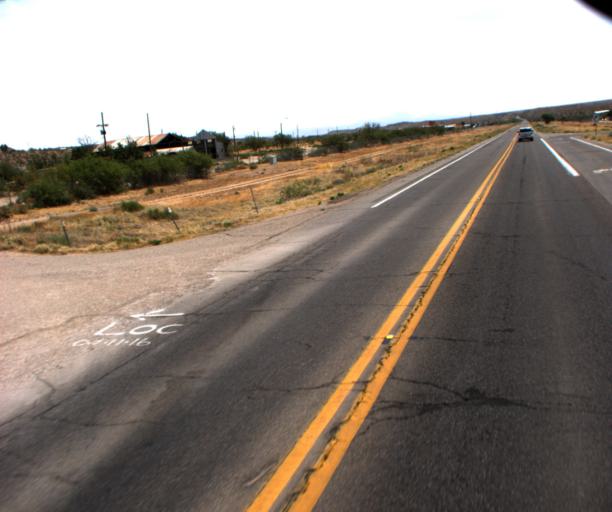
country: US
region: Arizona
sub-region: Gila County
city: Globe
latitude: 33.3544
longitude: -110.6623
